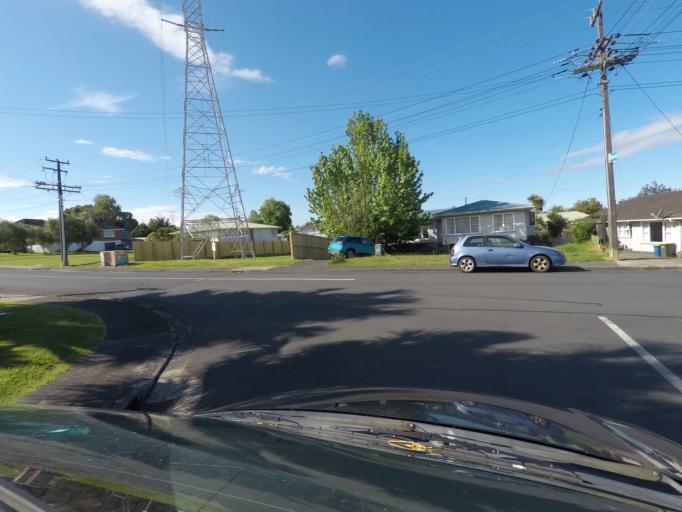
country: NZ
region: Auckland
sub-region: Auckland
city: Rosebank
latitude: -36.8674
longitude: 174.6492
